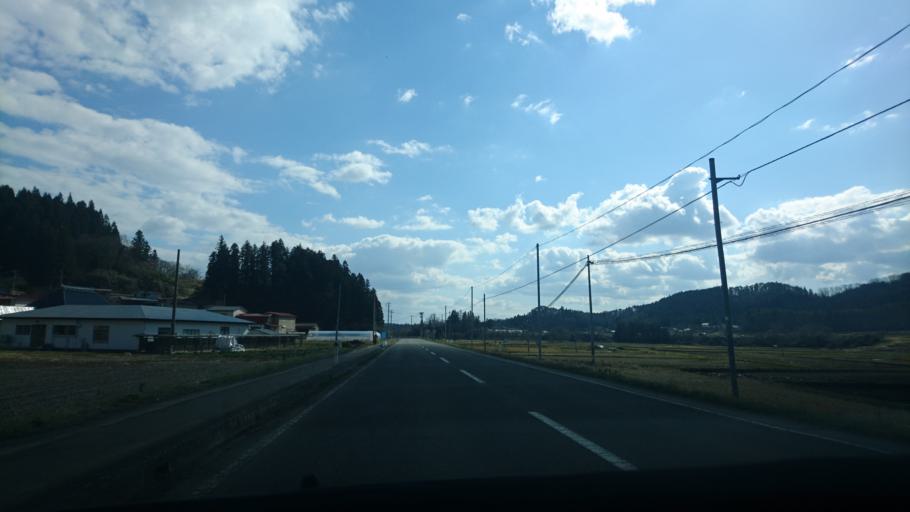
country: JP
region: Iwate
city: Kitakami
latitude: 39.2480
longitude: 141.2035
